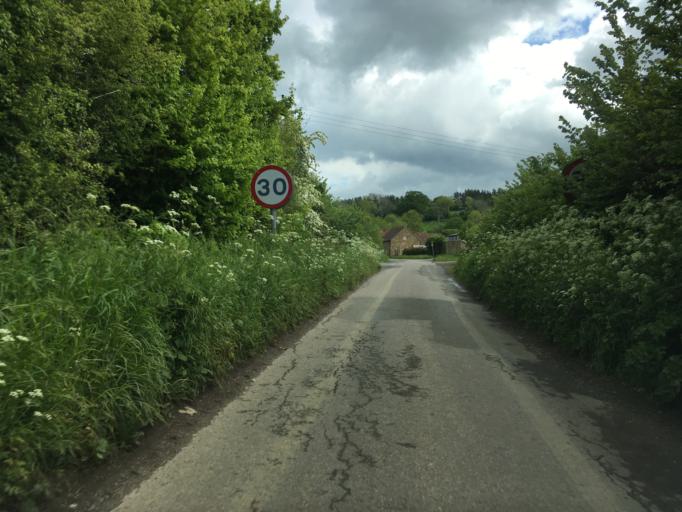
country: GB
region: England
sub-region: Gloucestershire
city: Dursley
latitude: 51.6821
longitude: -2.3961
